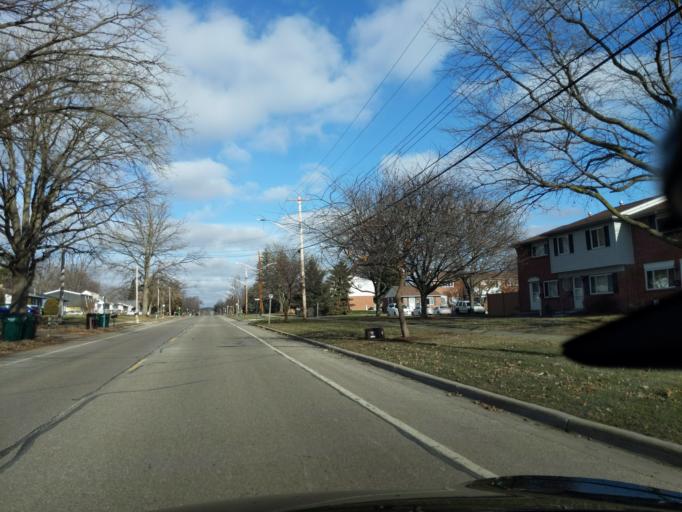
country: US
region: Michigan
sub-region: Ingham County
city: Lansing
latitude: 42.6719
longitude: -84.5726
